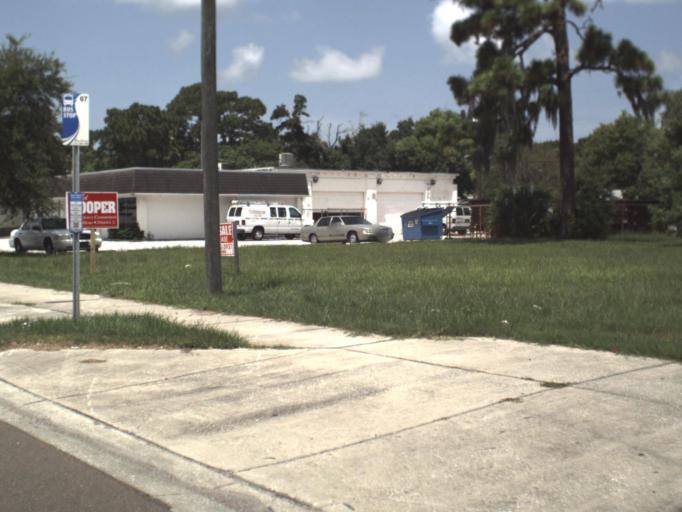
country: US
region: Florida
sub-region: Pinellas County
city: Clearwater
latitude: 27.9681
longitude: -82.7573
